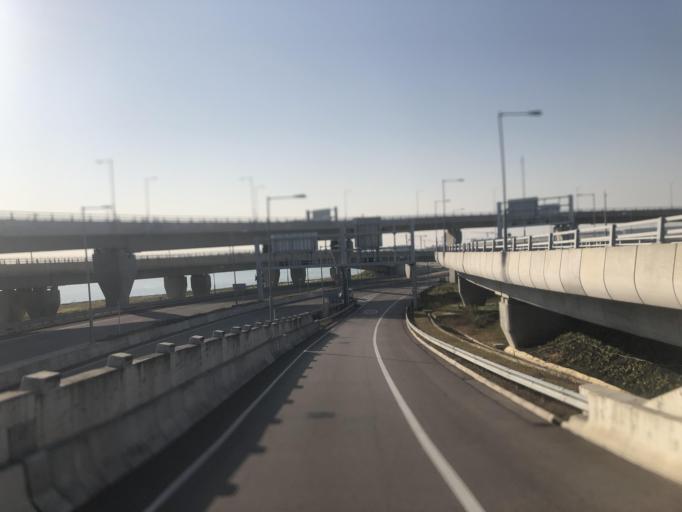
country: HK
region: Tuen Mun
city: Tuen Mun
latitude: 22.3120
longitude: 113.9552
